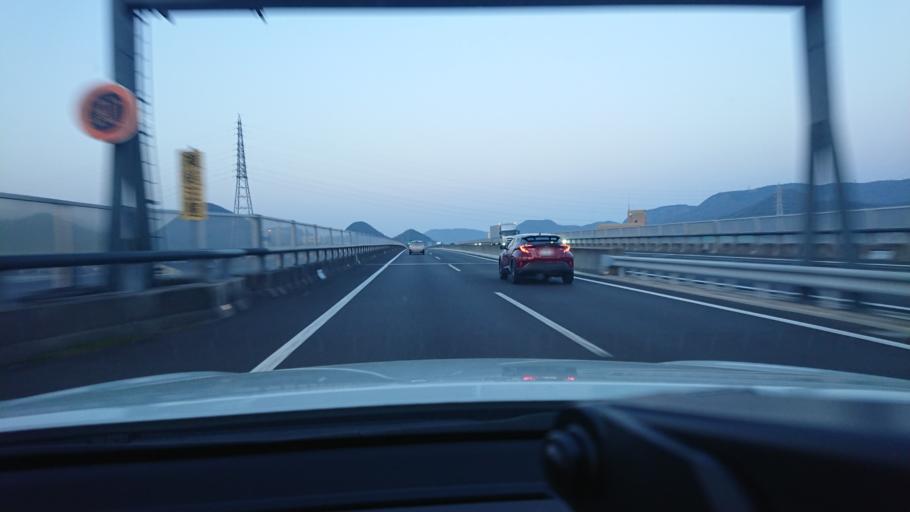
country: JP
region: Kagawa
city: Takamatsu-shi
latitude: 34.3072
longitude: 134.0115
